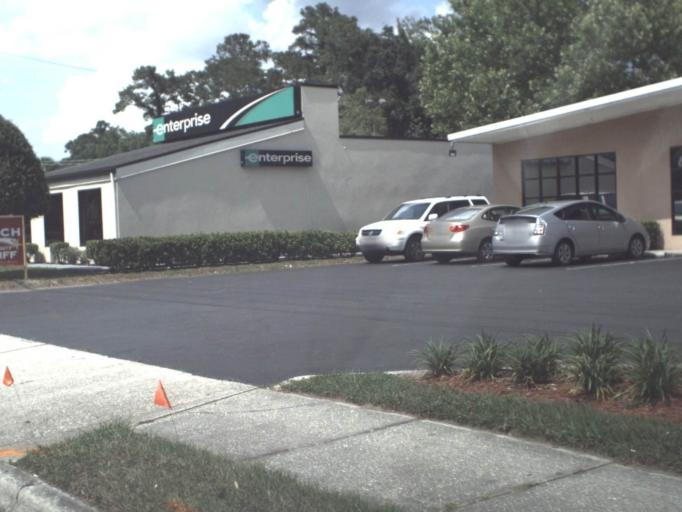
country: US
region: Florida
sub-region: Clay County
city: Orange Park
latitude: 30.1735
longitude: -81.7013
